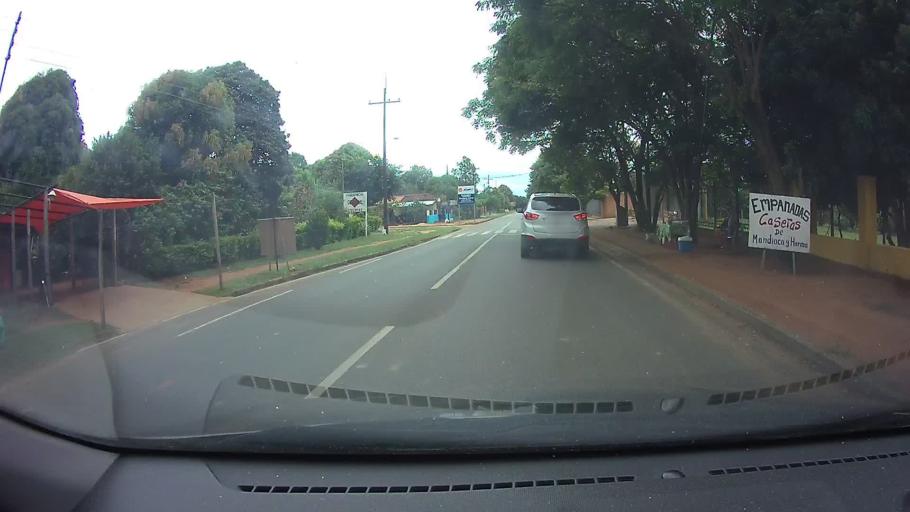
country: PY
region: Central
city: Nueva Italia
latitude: -25.6120
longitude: -57.4620
